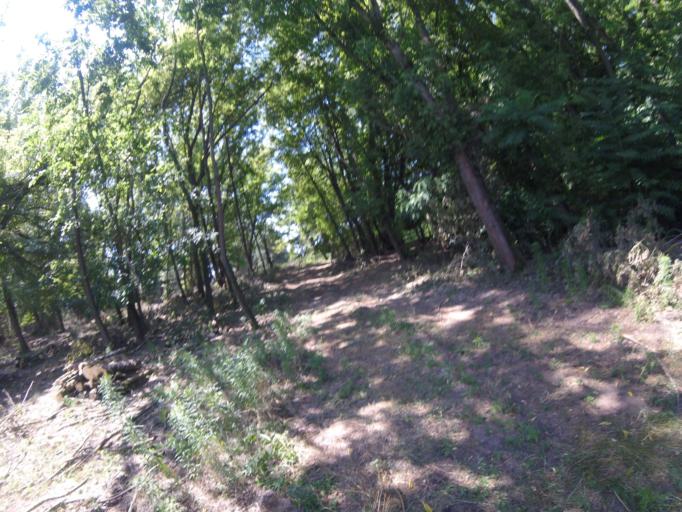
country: HU
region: Bacs-Kiskun
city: Jaszszentlaszlo
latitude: 46.6228
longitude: 19.7152
